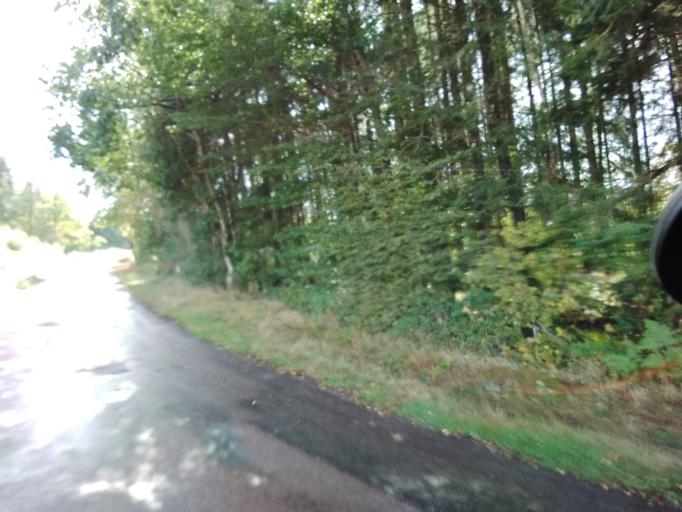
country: FR
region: Bourgogne
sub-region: Departement de la Nievre
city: Lormes
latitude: 47.3093
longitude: 3.8915
